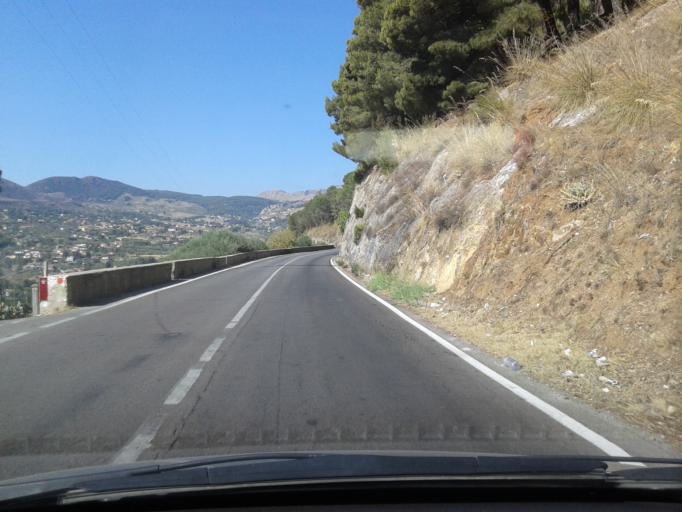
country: IT
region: Sicily
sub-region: Palermo
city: Cannizzaro-Favara
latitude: 38.0555
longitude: 13.2537
